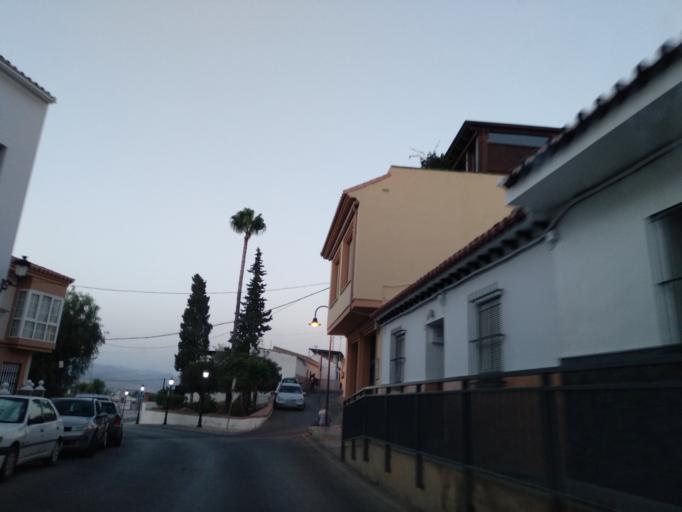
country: ES
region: Andalusia
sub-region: Provincia de Malaga
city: Cartama
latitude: 36.7126
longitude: -4.6277
